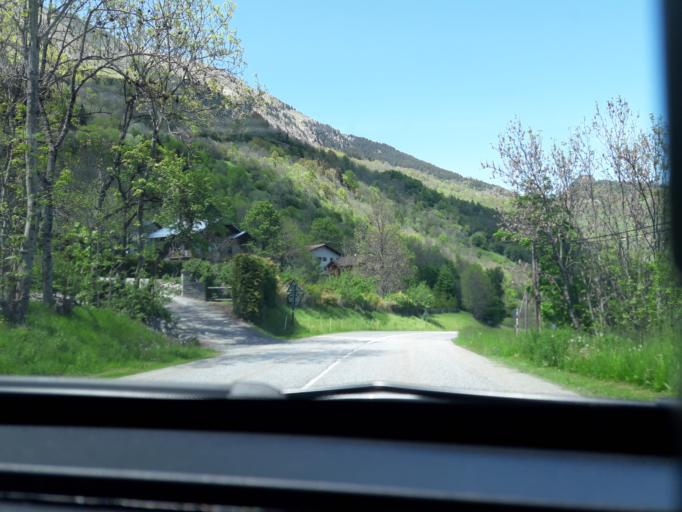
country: FR
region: Rhone-Alpes
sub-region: Departement de la Savoie
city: Salins-les-Thermes
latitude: 45.4378
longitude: 6.4901
